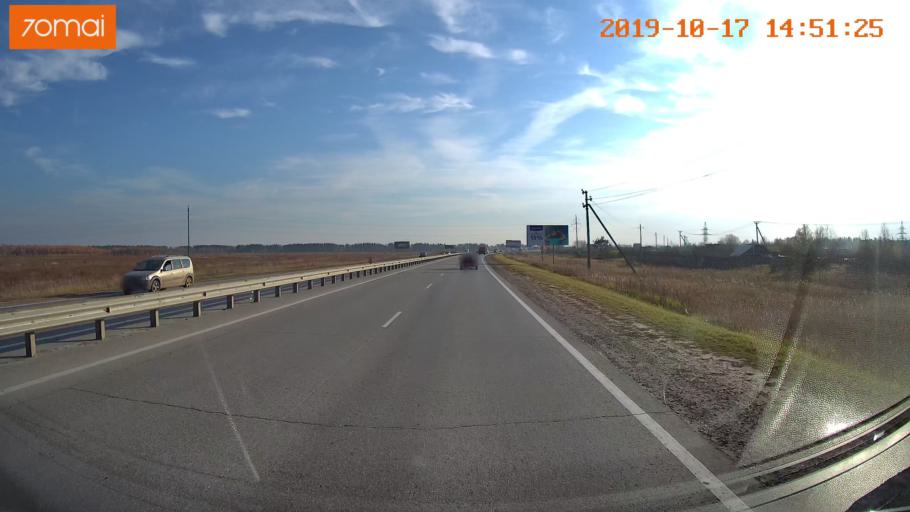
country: RU
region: Rjazan
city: Polyany
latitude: 54.7197
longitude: 39.8480
